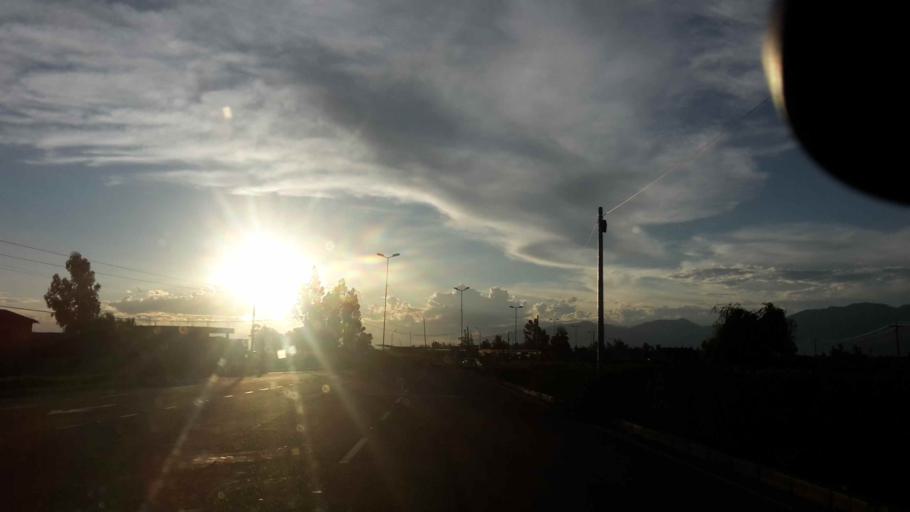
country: BO
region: Cochabamba
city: Arani
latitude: -17.5659
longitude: -65.7858
